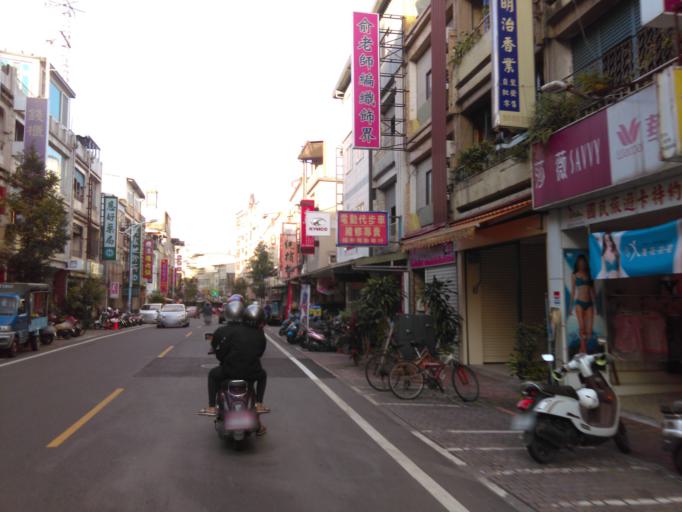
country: TW
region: Taiwan
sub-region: Yilan
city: Yilan
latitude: 24.8188
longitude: 121.7697
